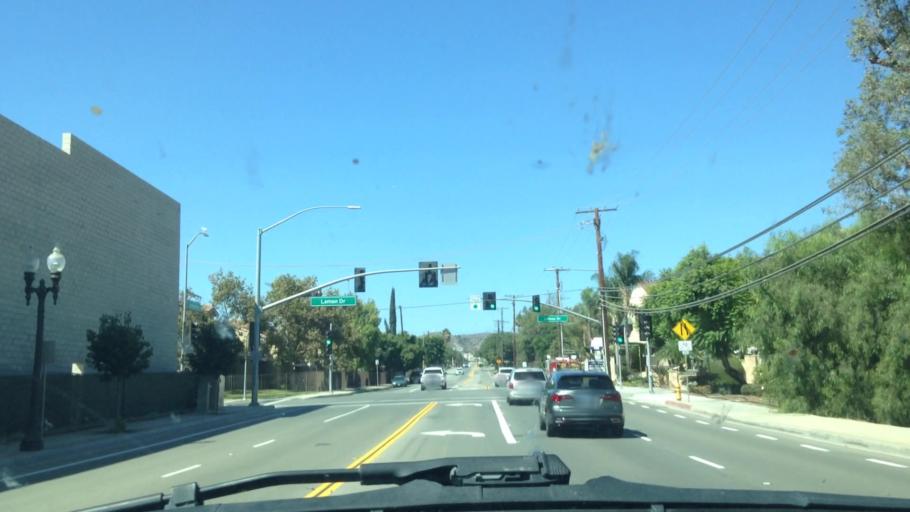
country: US
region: California
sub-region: Orange County
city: Yorba Linda
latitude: 33.8909
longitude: -117.8113
